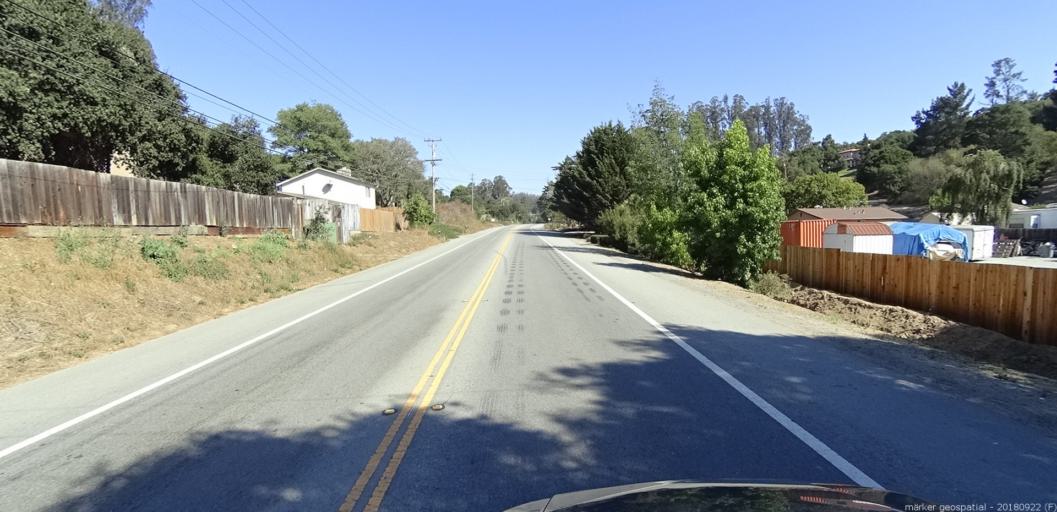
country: US
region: California
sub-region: Monterey County
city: Prunedale
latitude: 36.8135
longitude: -121.6736
